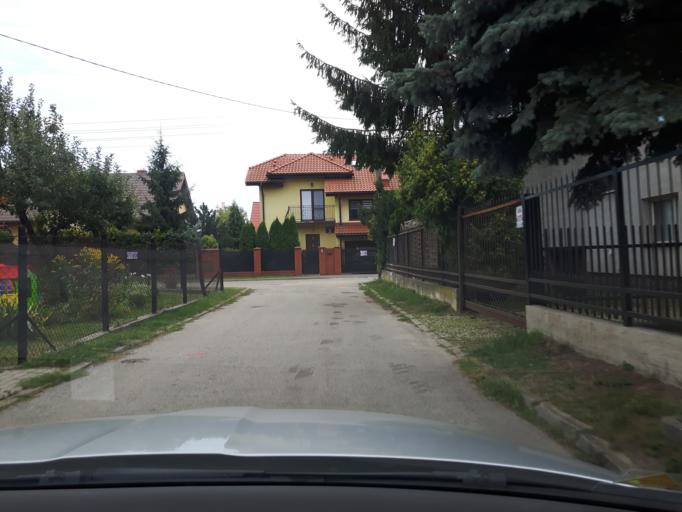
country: PL
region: Masovian Voivodeship
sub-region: Powiat wolominski
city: Zabki
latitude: 52.2915
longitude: 21.1061
